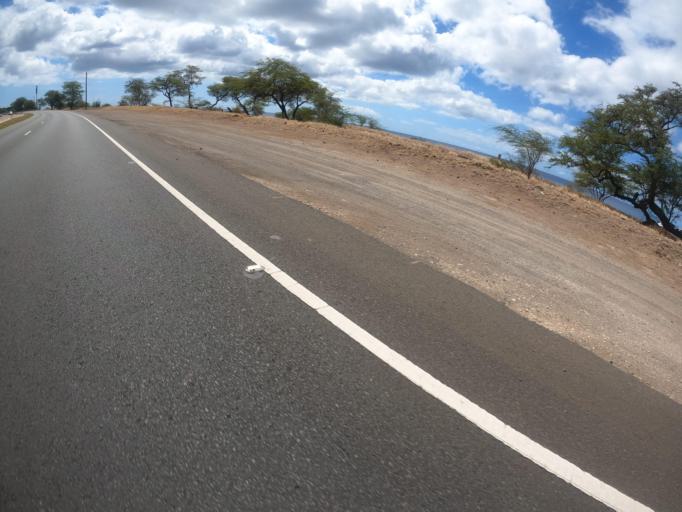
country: US
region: Hawaii
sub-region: Honolulu County
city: Makakilo
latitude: 21.3524
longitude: -158.1298
